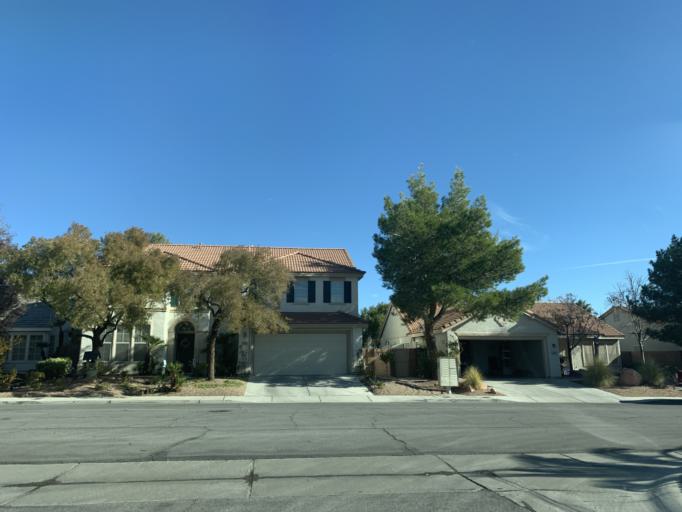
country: US
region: Nevada
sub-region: Clark County
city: Summerlin South
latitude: 36.1236
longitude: -115.3049
